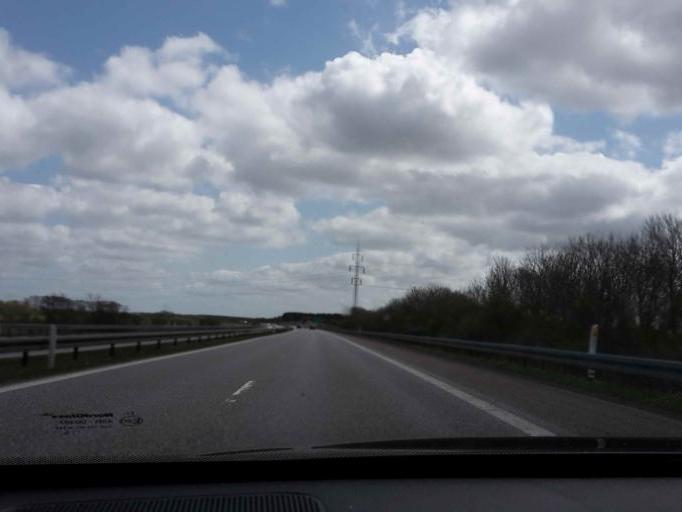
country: DK
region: South Denmark
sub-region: Esbjerg Kommune
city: Tjaereborg
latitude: 55.5133
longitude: 8.6327
